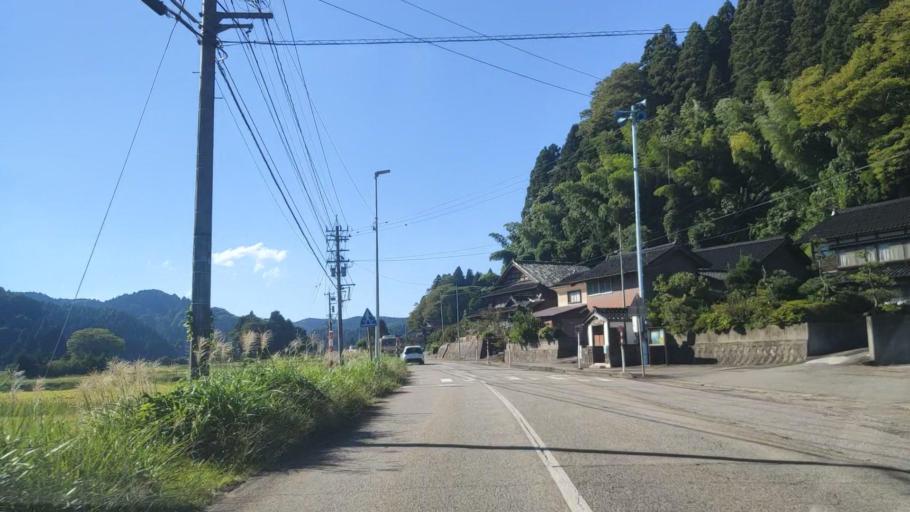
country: JP
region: Ishikawa
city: Nanao
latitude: 37.2781
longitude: 137.0516
